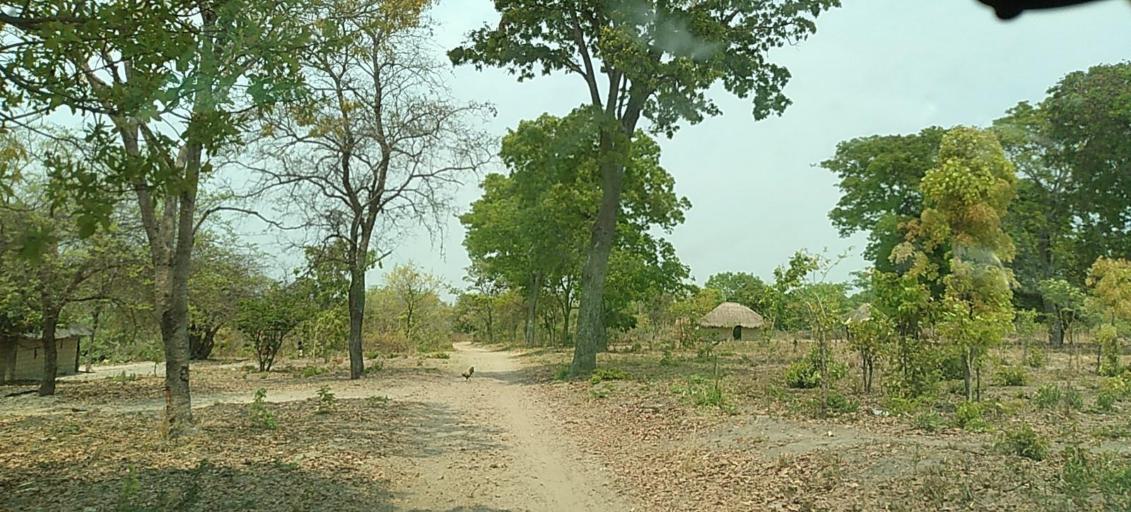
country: ZM
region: North-Western
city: Kabompo
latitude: -13.5366
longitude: 24.4566
